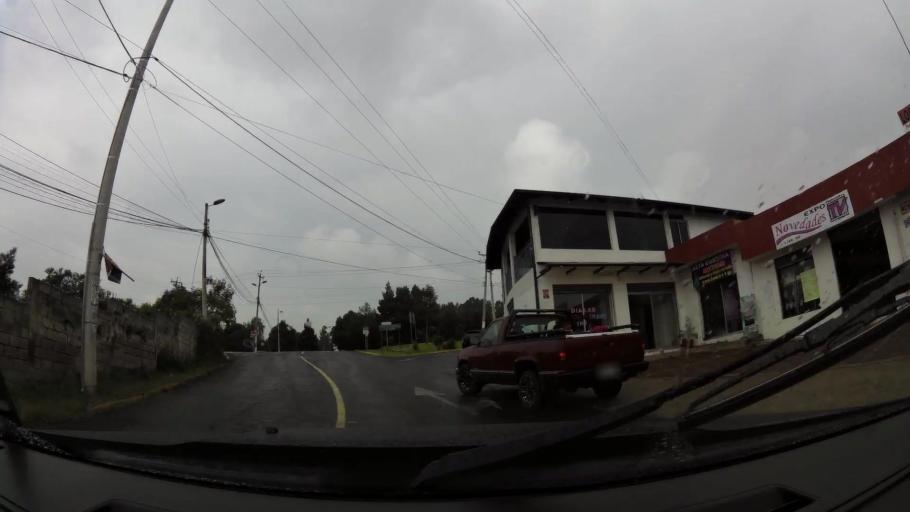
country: EC
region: Pichincha
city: Sangolqui
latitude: -0.2830
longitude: -78.4691
